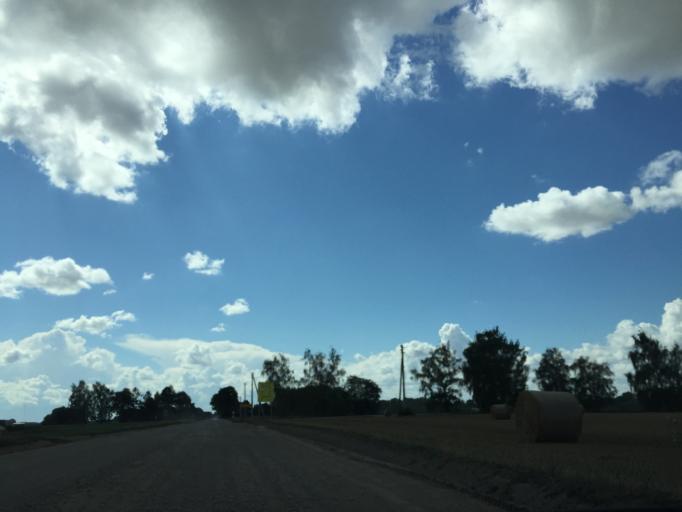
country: LV
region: Rundales
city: Pilsrundale
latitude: 56.3010
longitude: 23.9999
